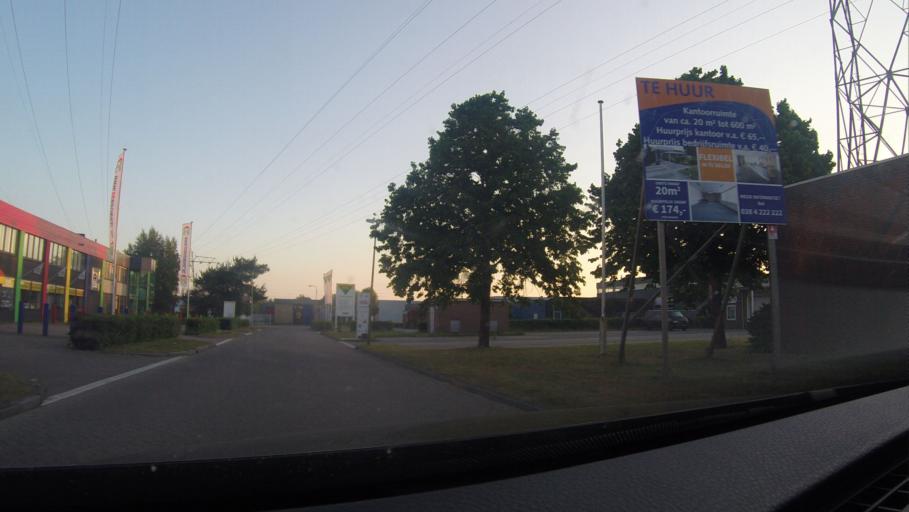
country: NL
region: Overijssel
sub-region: Gemeente Zwolle
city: Zwolle
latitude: 52.4973
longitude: 6.1264
